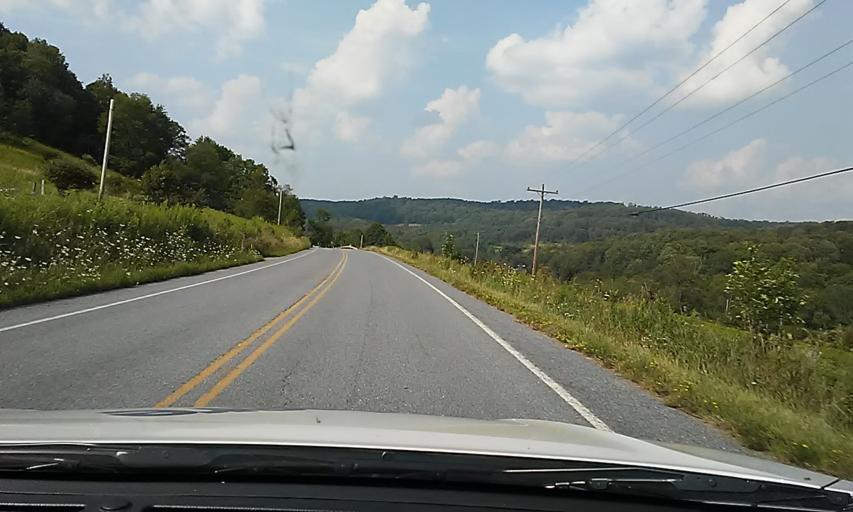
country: US
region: New York
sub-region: Allegany County
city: Wellsville
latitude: 41.9314
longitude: -77.8526
